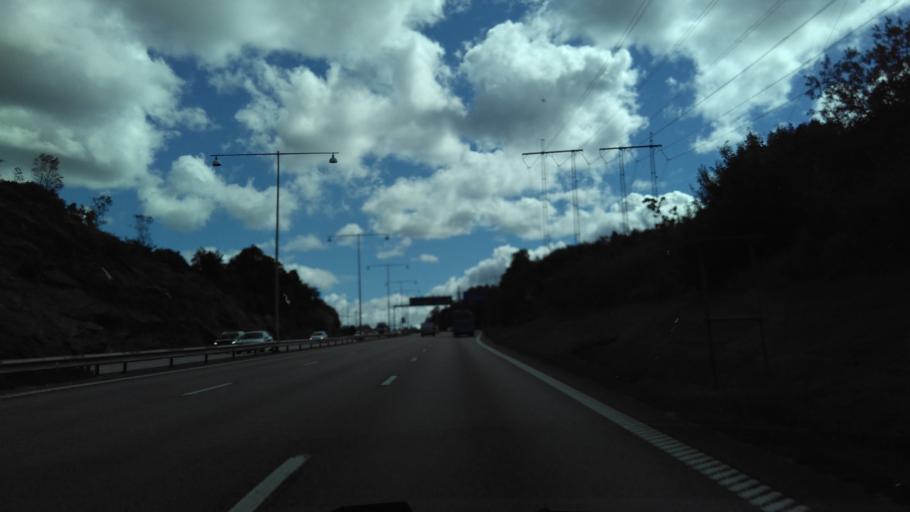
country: SE
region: Vaestra Goetaland
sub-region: Molndal
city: Moelndal
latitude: 57.6803
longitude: 12.0198
